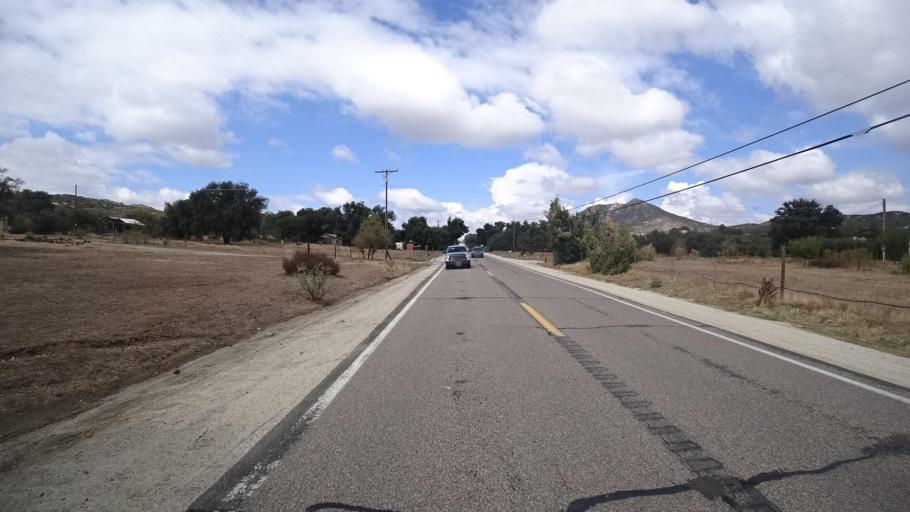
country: US
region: California
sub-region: San Diego County
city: Campo
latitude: 32.6650
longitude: -116.4881
